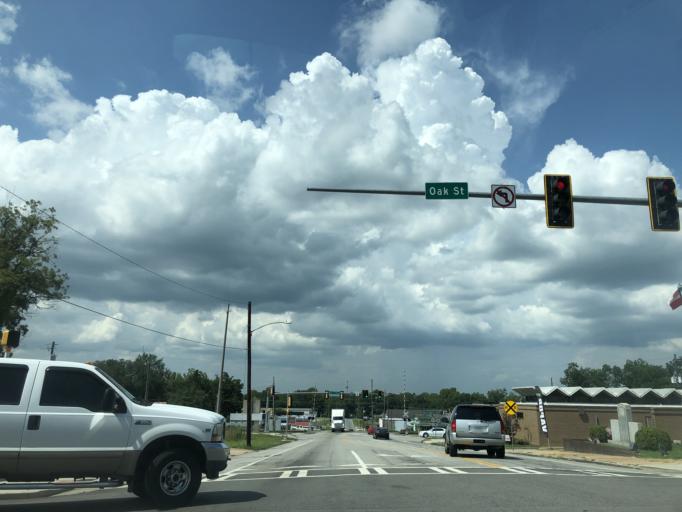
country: US
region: Georgia
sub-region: Telfair County
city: McRae
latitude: 32.0681
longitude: -82.9009
